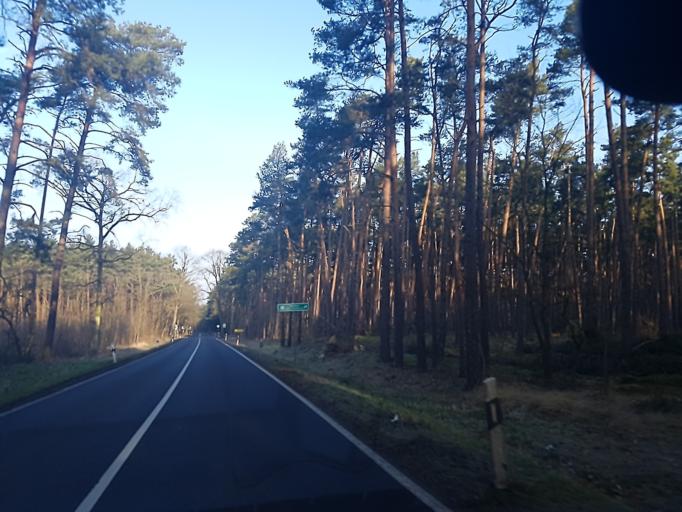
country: DE
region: Brandenburg
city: Golzow
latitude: 52.2727
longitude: 12.6355
